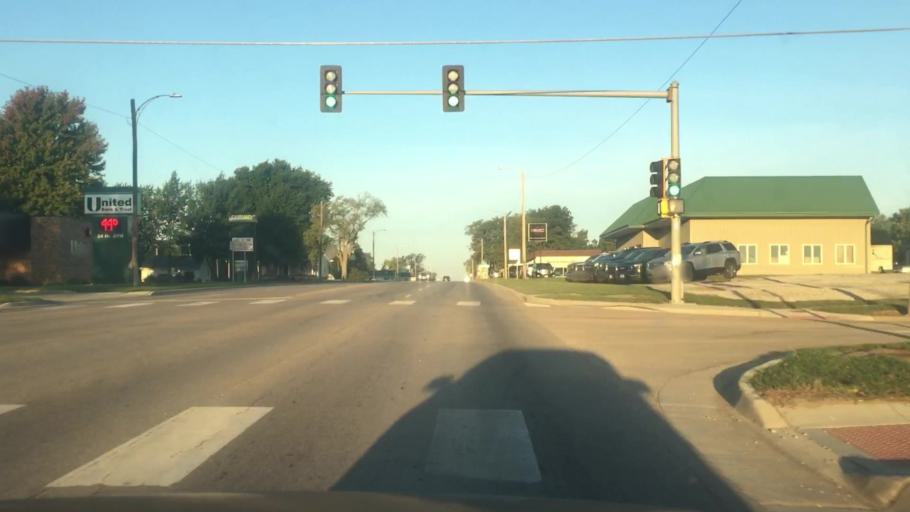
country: US
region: Kansas
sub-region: Nemaha County
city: Seneca
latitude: 39.8413
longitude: -96.0640
